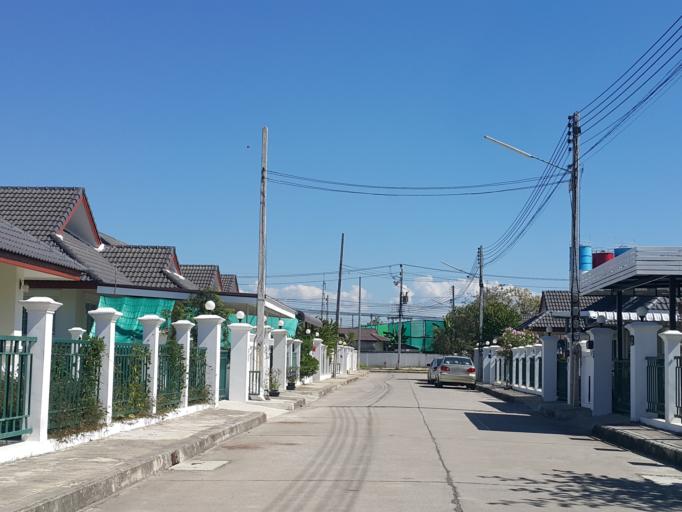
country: TH
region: Chiang Mai
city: San Sai
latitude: 18.7955
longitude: 99.0642
